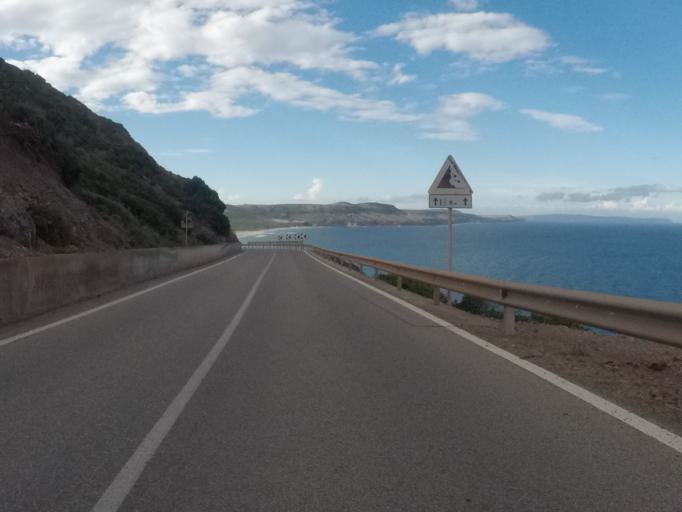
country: IT
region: Sardinia
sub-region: Provincia di Carbonia-Iglesias
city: Gonnesa
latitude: 39.3013
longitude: 8.4360
